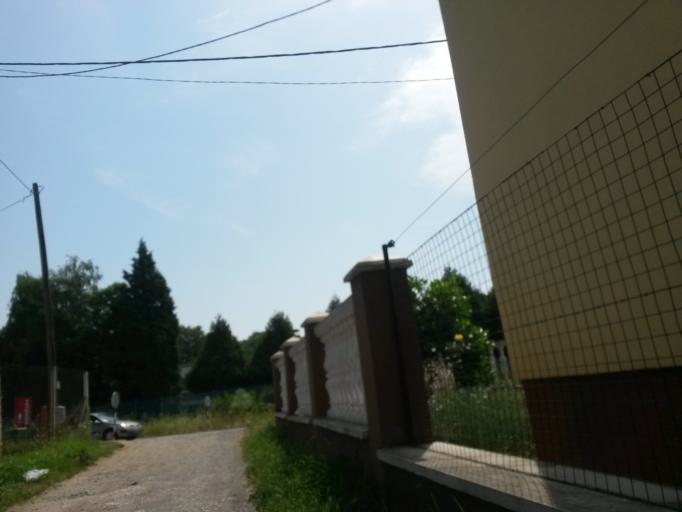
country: HR
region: Osjecko-Baranjska
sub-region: Grad Osijek
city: Osijek
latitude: 45.5436
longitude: 18.6761
